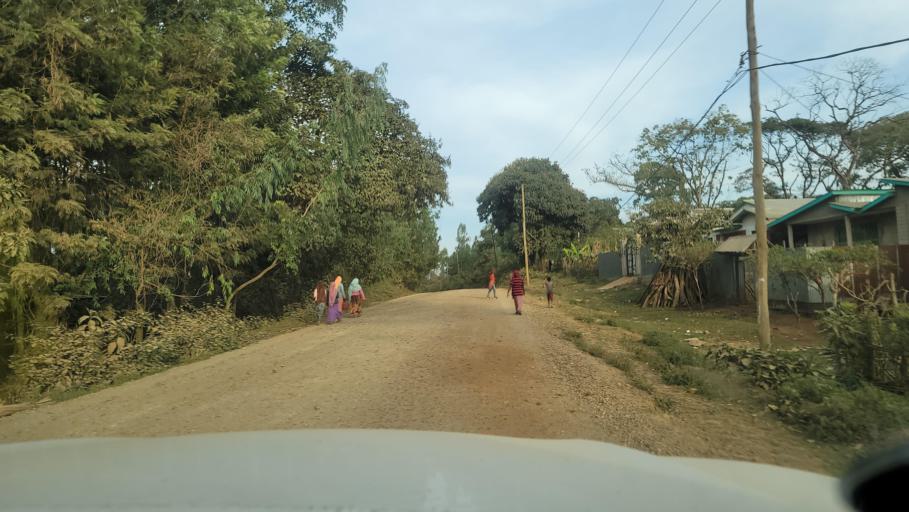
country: ET
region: Oromiya
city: Agaro
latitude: 7.8395
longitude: 36.5455
